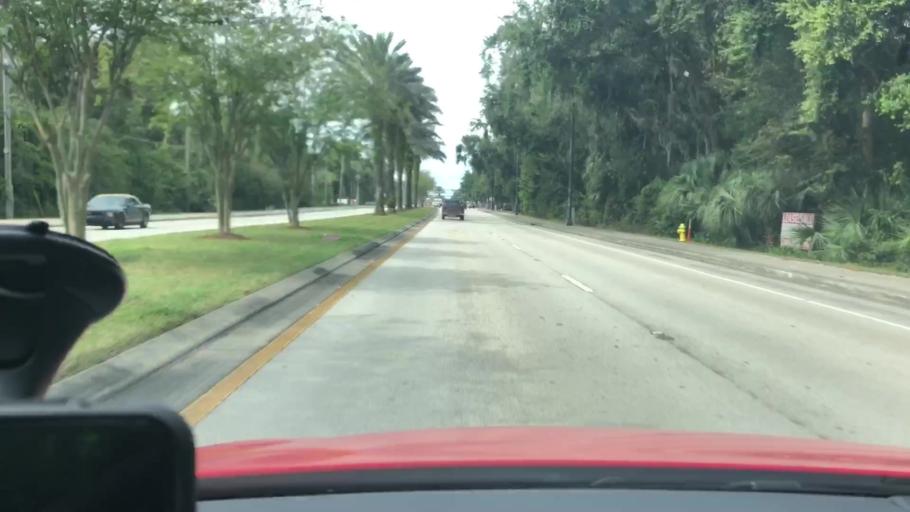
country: US
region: Florida
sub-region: Volusia County
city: Port Orange
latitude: 29.1222
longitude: -81.0021
